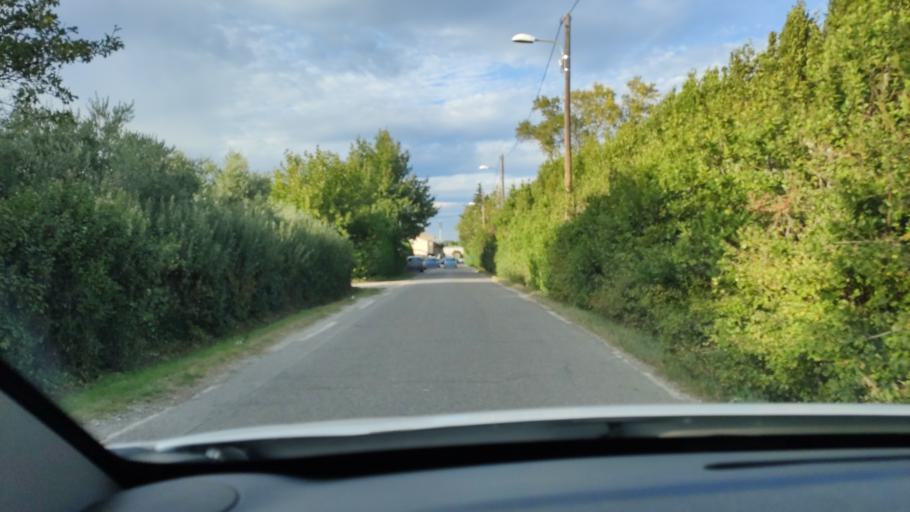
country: FR
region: Provence-Alpes-Cote d'Azur
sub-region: Departement du Vaucluse
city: Montfavet
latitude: 43.9229
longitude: 4.8436
